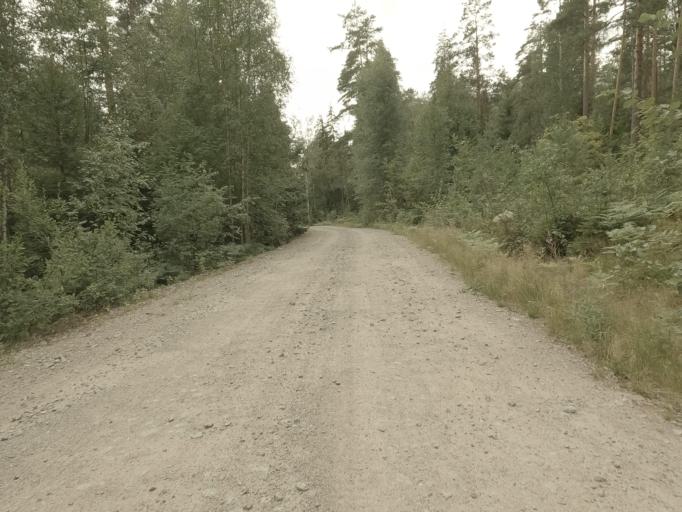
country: RU
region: Leningrad
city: Kamennogorsk
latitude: 60.9877
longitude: 29.1845
